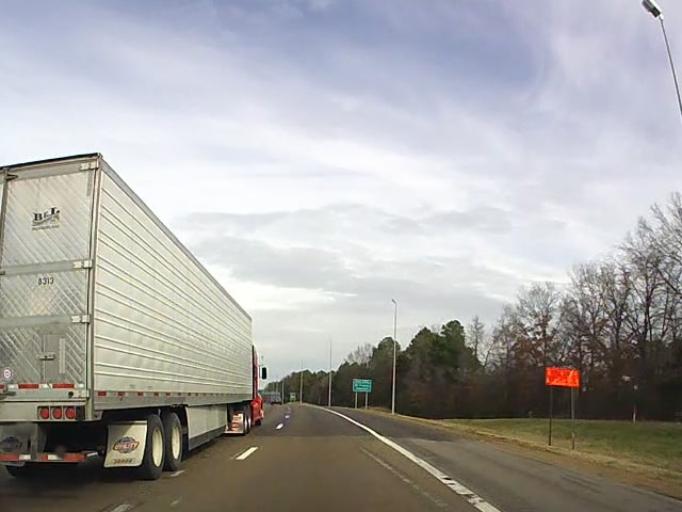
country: US
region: Tennessee
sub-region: Shelby County
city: Germantown
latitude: 35.0924
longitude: -89.8701
